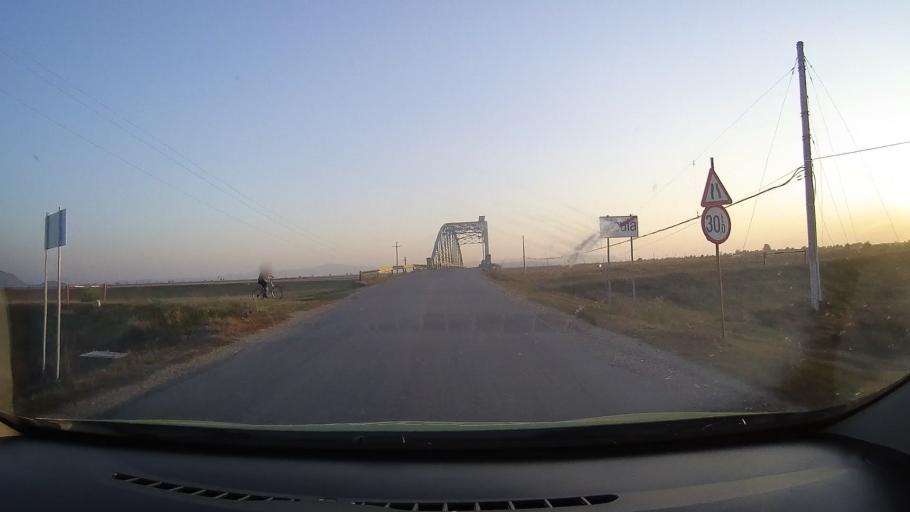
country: RO
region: Arad
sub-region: Comuna Sicula
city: Sicula
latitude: 46.4311
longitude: 21.7571
